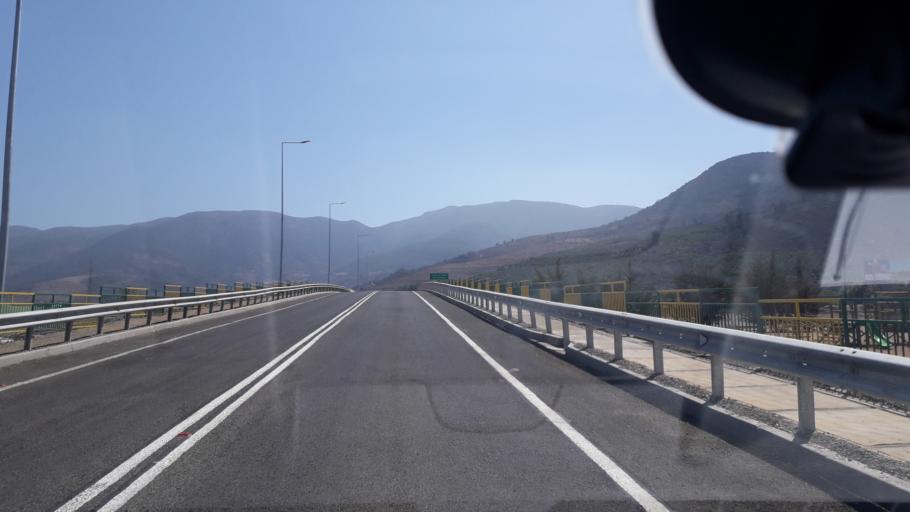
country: CL
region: Valparaiso
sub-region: Provincia de Quillota
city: Hacienda La Calera
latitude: -32.8172
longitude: -71.2416
